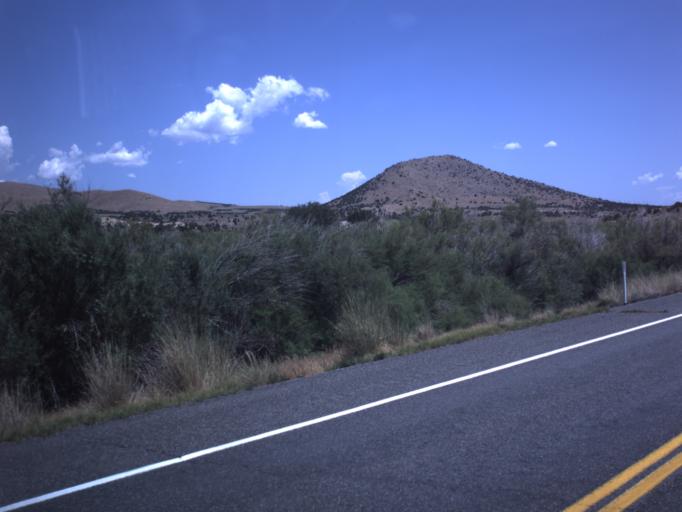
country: US
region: Utah
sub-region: Juab County
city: Nephi
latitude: 39.5797
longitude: -112.1744
